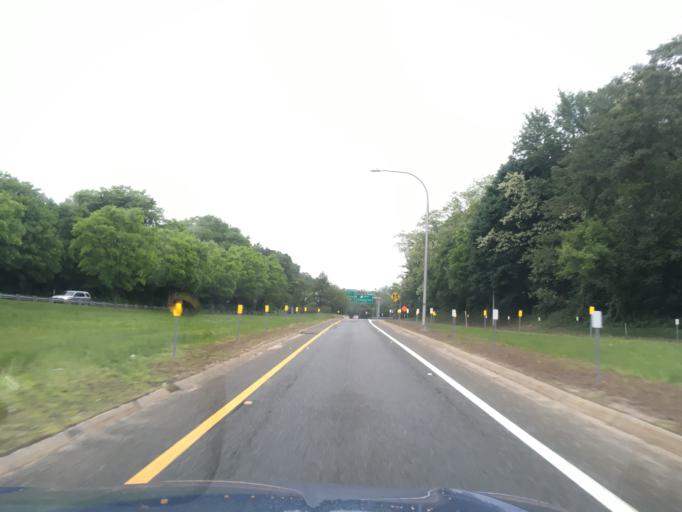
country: US
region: Rhode Island
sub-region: Providence County
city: Cranston
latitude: 41.7764
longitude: -71.4180
